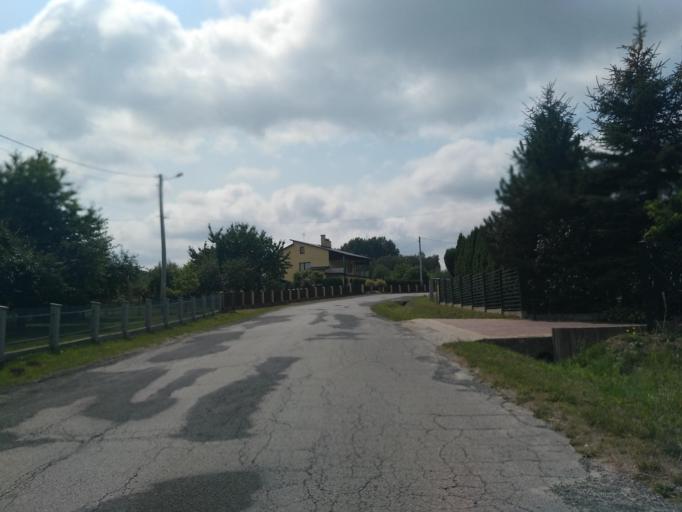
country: PL
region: Subcarpathian Voivodeship
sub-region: Powiat lancucki
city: Kraczkowa
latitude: 50.0168
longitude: 22.1719
